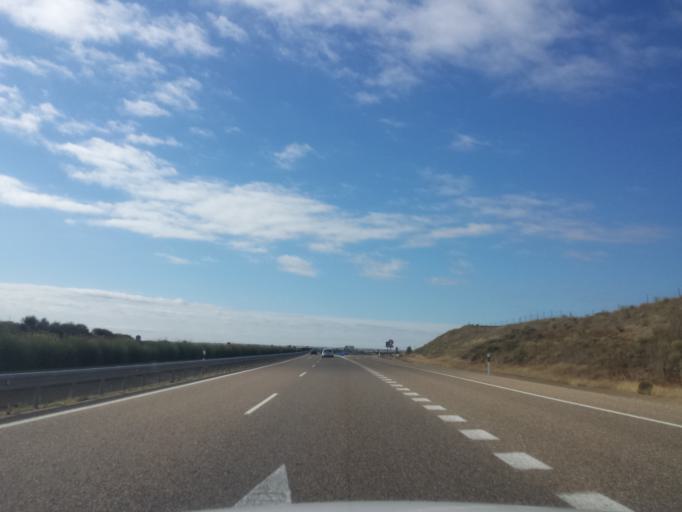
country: ES
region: Castille and Leon
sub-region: Provincia de Leon
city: Toral de los Guzmanes
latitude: 42.2506
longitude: -5.5937
